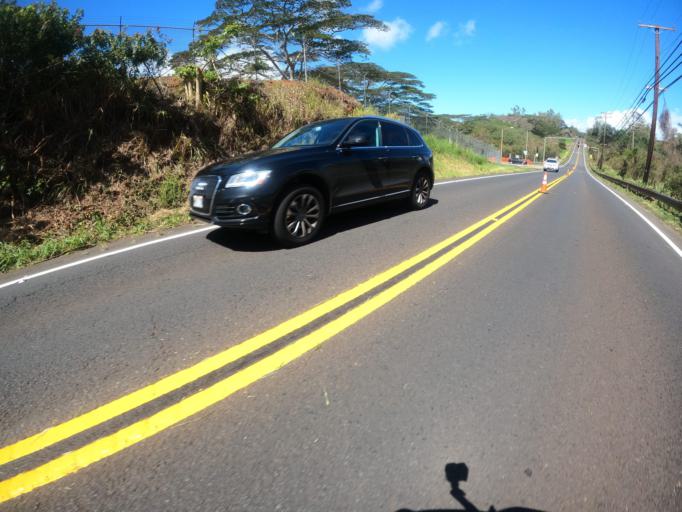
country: US
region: Hawaii
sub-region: Honolulu County
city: Schofield Barracks
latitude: 21.4753
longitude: -158.0511
